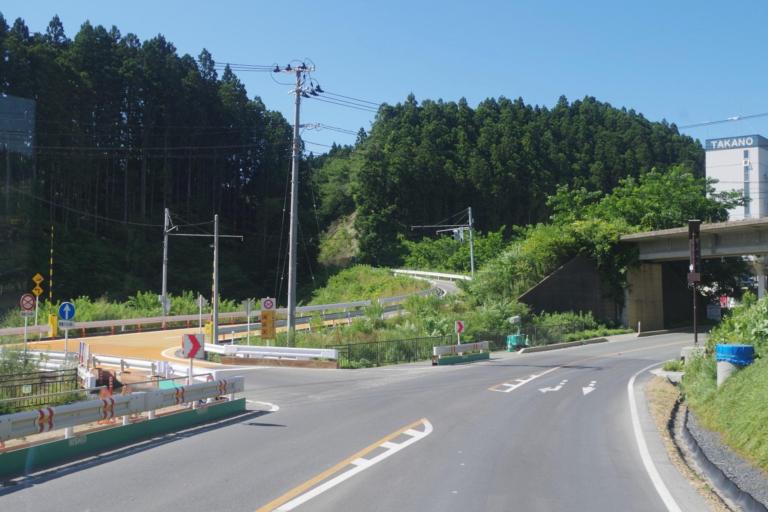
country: JP
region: Miyagi
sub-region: Oshika Gun
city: Onagawa Cho
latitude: 38.6726
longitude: 141.4427
